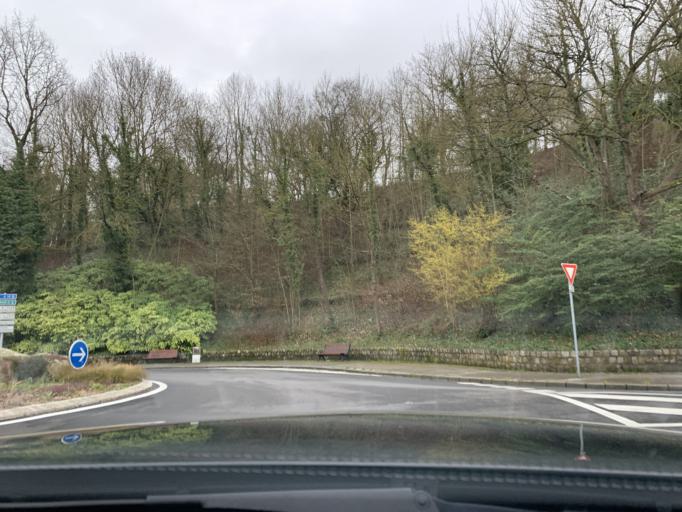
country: FR
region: Picardie
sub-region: Departement de l'Oise
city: Beauvais
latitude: 49.4255
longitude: 2.0816
